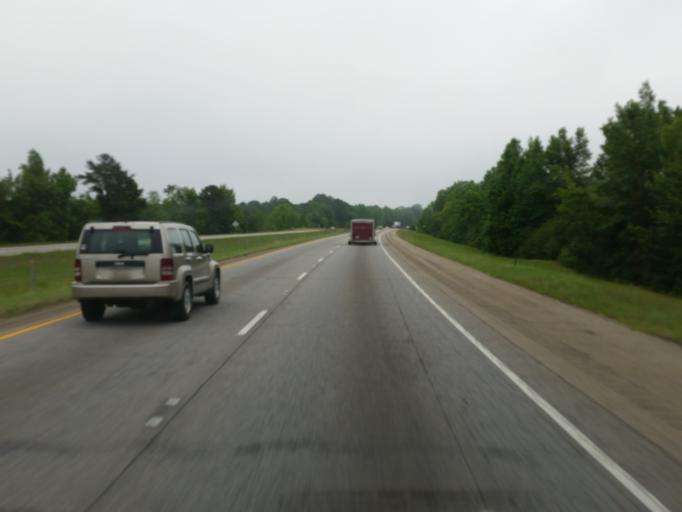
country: US
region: Louisiana
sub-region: Webster Parish
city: Minden
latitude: 32.5941
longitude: -93.3204
